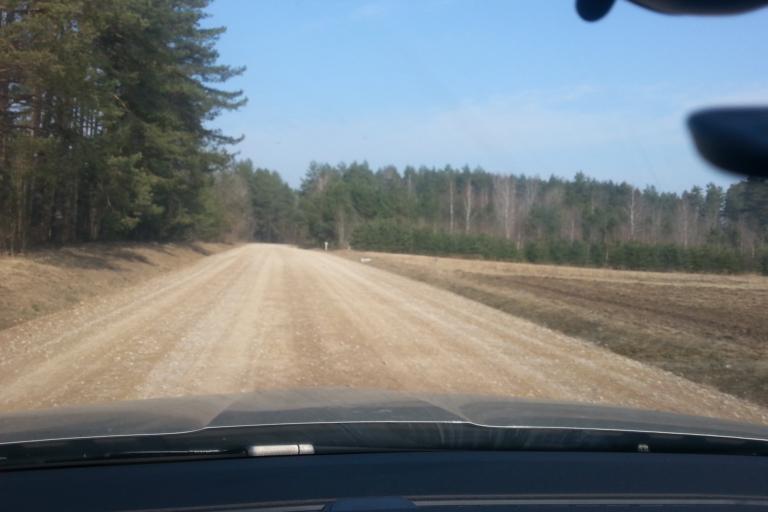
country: LT
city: Trakai
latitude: 54.5736
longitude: 24.9681
